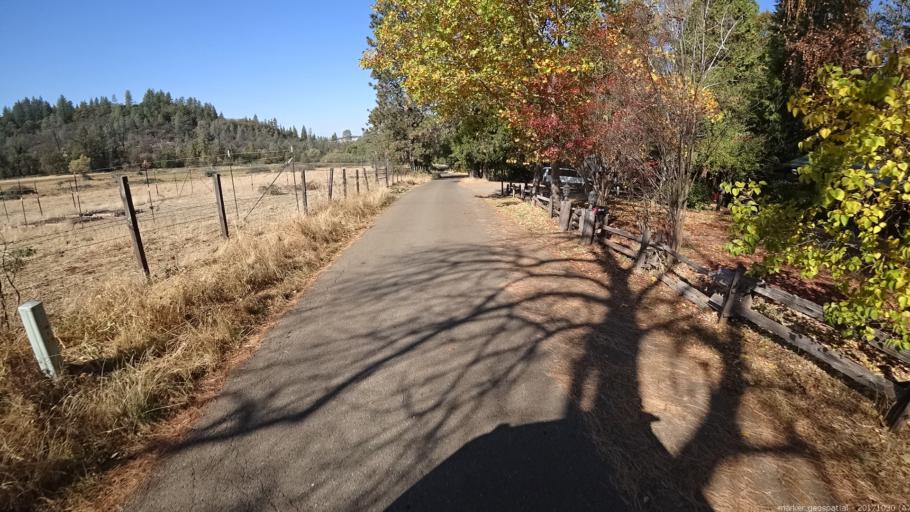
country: US
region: California
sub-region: Shasta County
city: Shingletown
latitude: 40.5254
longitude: -121.9231
